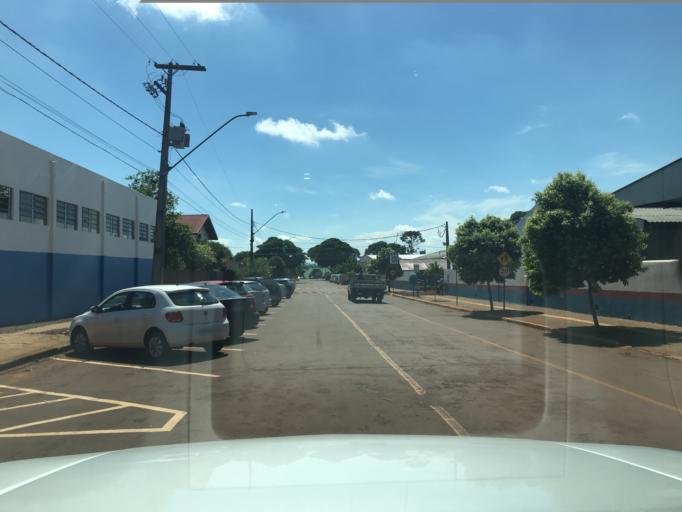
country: BR
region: Parana
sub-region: Palotina
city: Palotina
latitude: -24.2844
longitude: -53.8357
